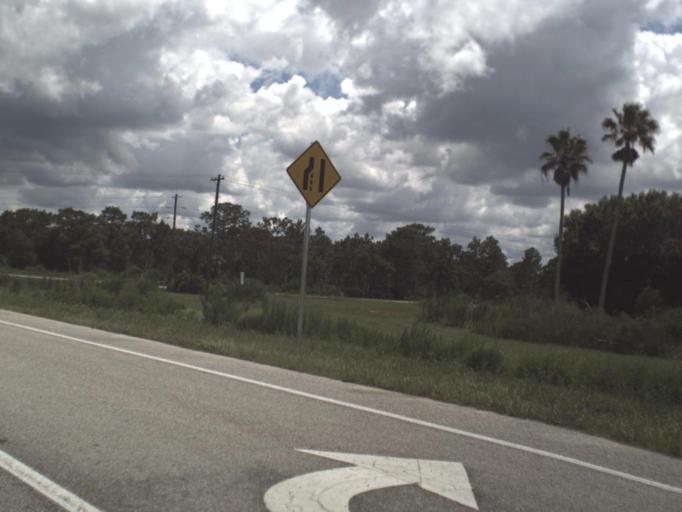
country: US
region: Florida
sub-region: Polk County
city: Babson Park
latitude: 27.8066
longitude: -81.3173
